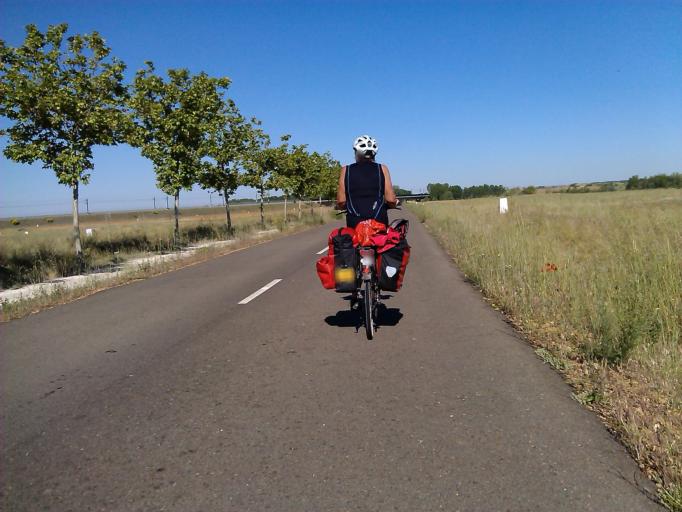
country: ES
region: Castille and Leon
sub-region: Provincia de Leon
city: Calzada del Coto
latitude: 42.3842
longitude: -5.1012
